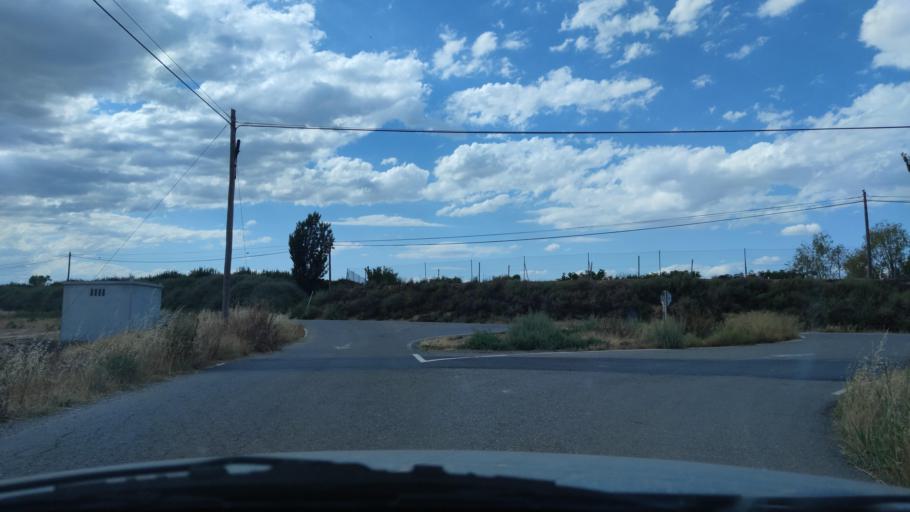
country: ES
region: Catalonia
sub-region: Provincia de Lleida
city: Alcarras
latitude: 41.6067
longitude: 0.5516
